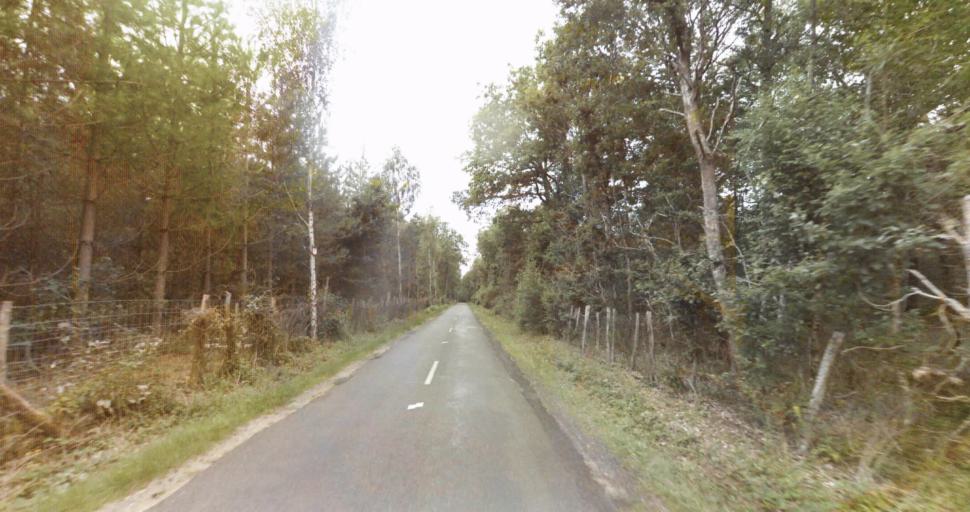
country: FR
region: Haute-Normandie
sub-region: Departement de l'Eure
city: Croth
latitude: 48.8573
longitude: 1.3606
